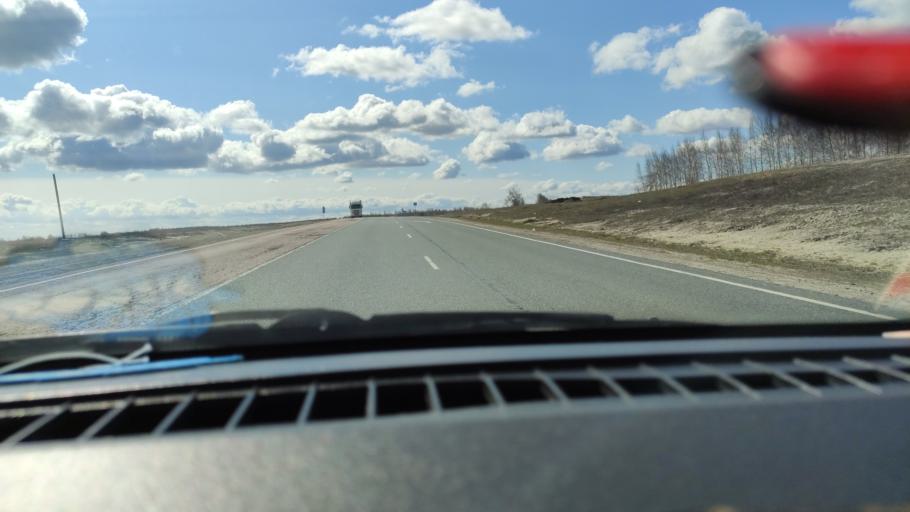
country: RU
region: Samara
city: Syzran'
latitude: 52.9537
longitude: 48.3072
